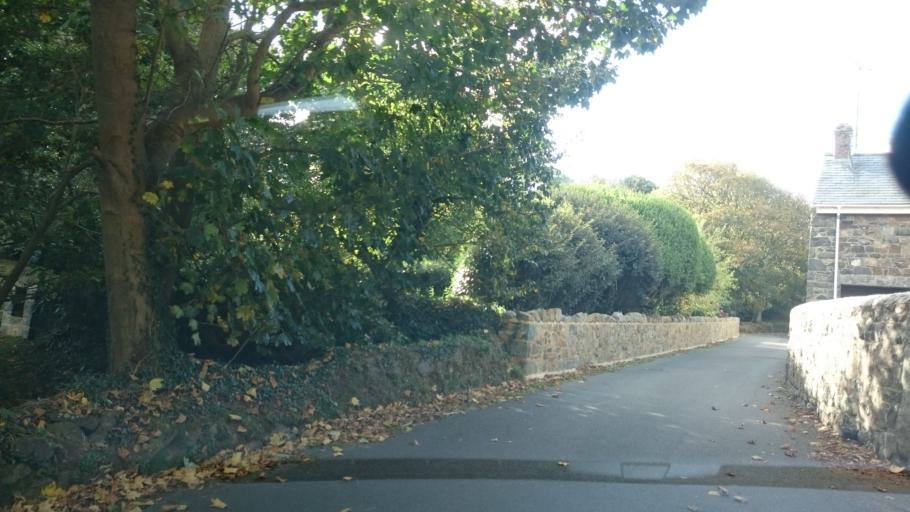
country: GG
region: St Peter Port
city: Saint Peter Port
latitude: 49.4313
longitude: -2.6632
